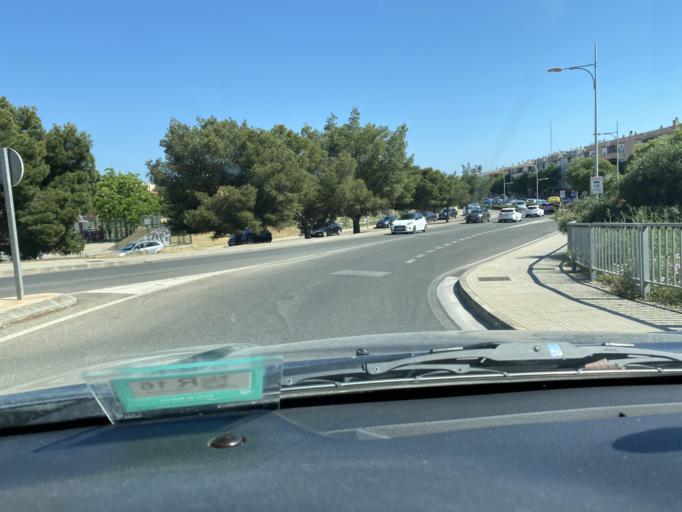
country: ES
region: Balearic Islands
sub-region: Illes Balears
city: Palma
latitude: 39.6055
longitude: 2.6860
